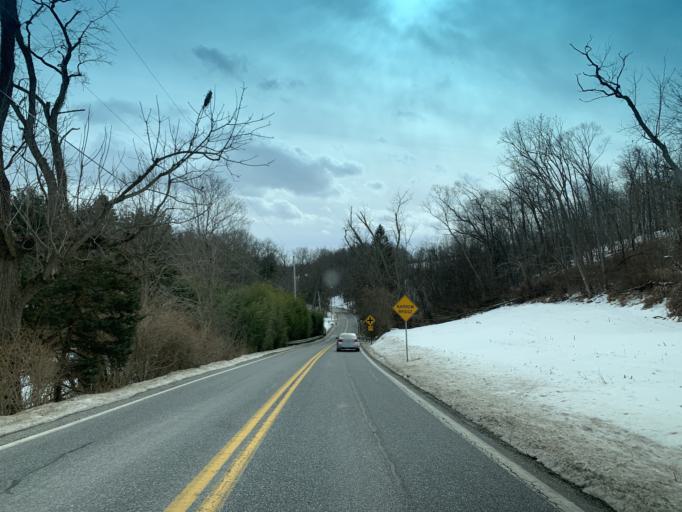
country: US
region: Pennsylvania
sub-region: York County
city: Shrewsbury
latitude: 39.8186
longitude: -76.6295
